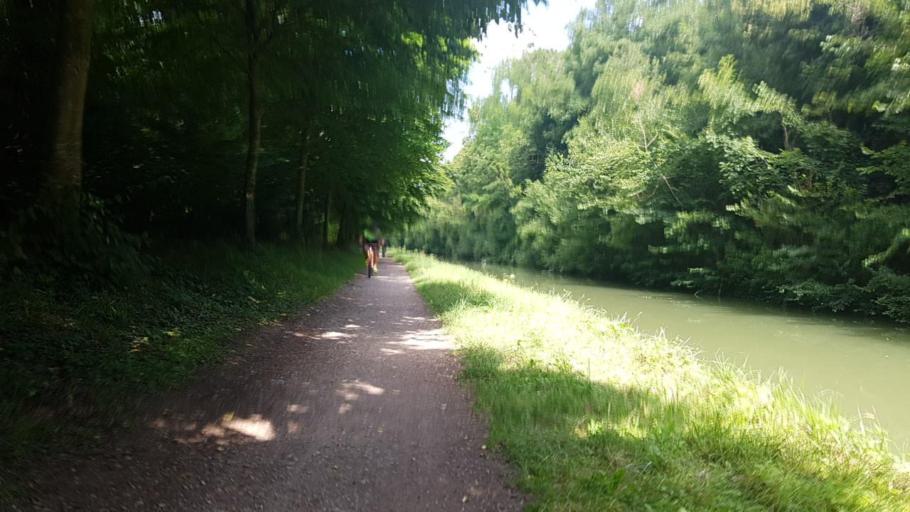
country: FR
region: Ile-de-France
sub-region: Departement de Seine-et-Marne
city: Claye-Souilly
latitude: 48.9507
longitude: 2.6908
